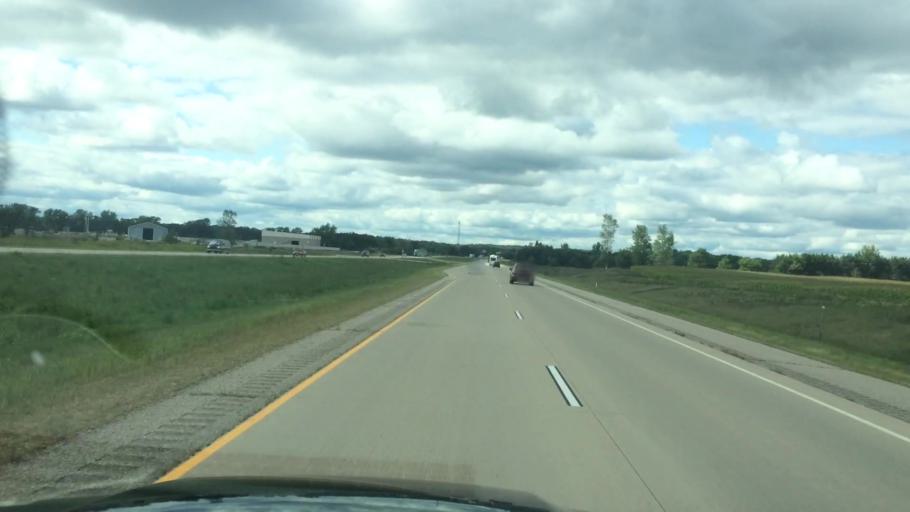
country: US
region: Wisconsin
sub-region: Portage County
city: Amherst
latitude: 44.5042
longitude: -89.4088
